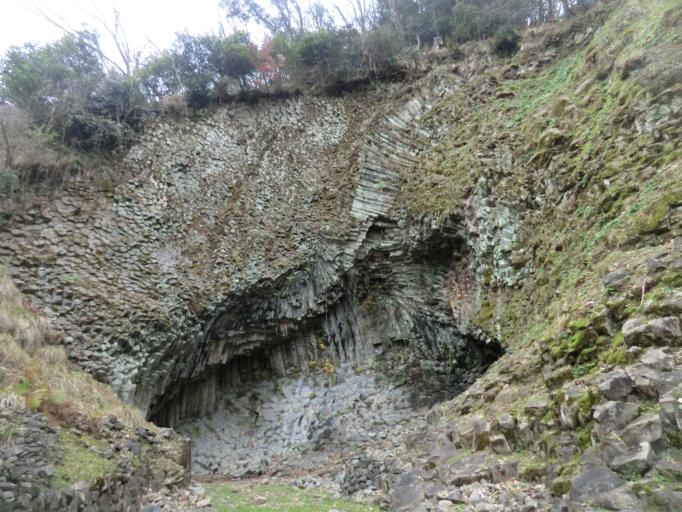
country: JP
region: Hyogo
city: Toyooka
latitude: 35.5895
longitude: 134.8045
